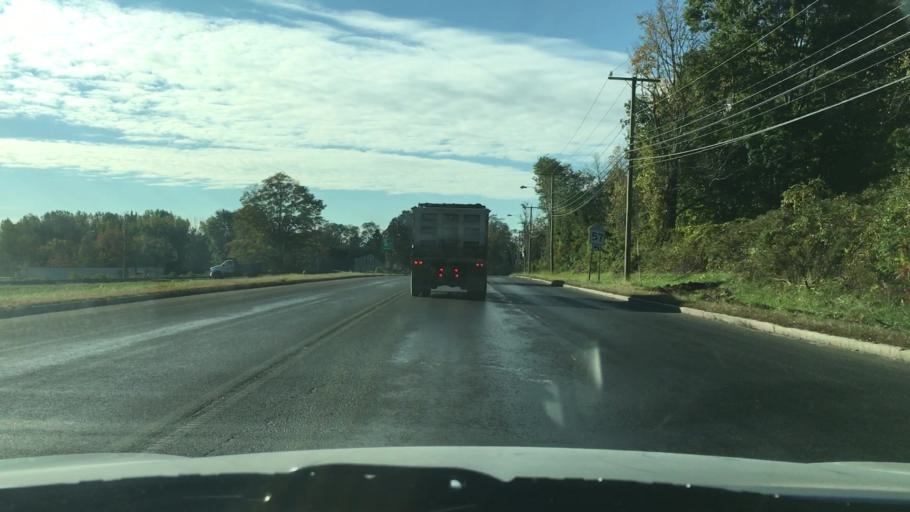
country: US
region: Massachusetts
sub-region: Hampden County
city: Agawam
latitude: 42.0563
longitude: -72.6756
